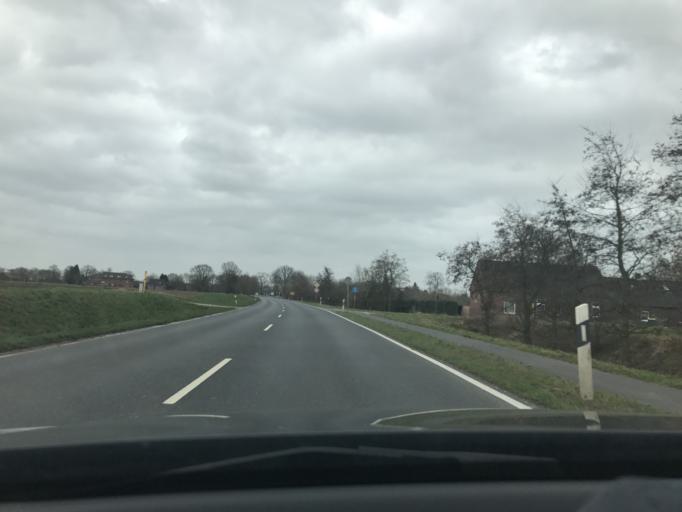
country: DE
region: North Rhine-Westphalia
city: Kempen
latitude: 51.3671
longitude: 6.4678
